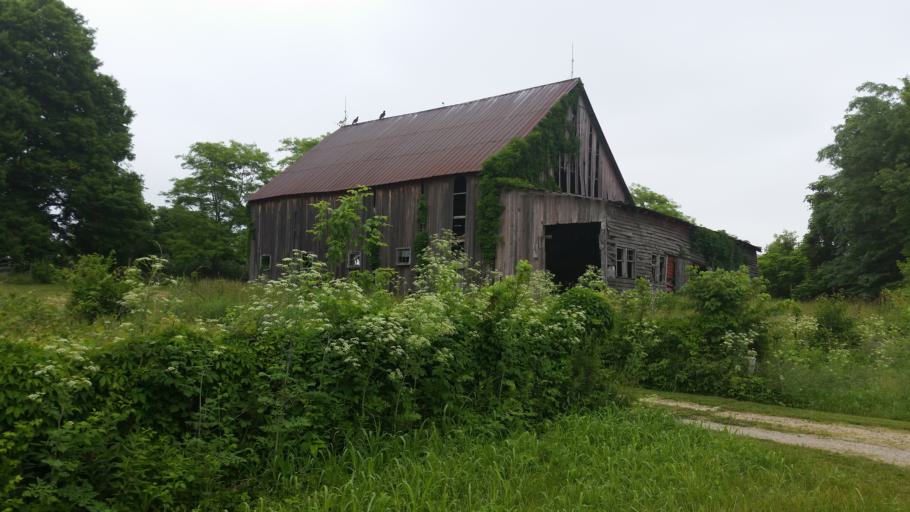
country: US
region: Ohio
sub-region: Highland County
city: Greenfield
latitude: 39.2300
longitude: -83.3609
